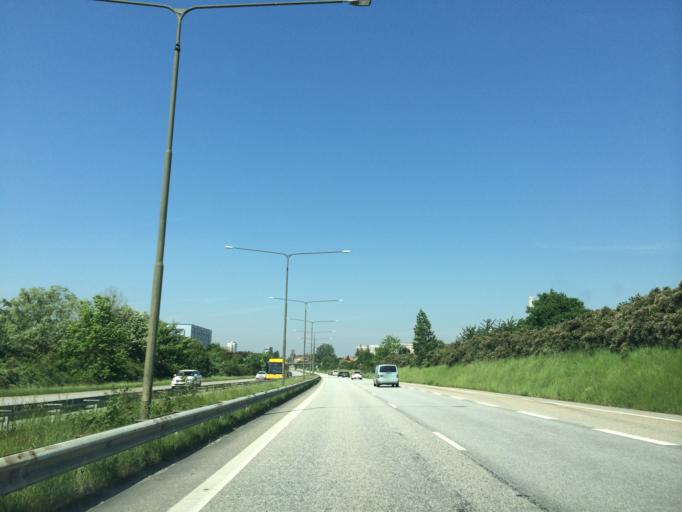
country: SE
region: Skane
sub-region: Malmo
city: Malmoe
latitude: 55.5700
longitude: 13.0040
